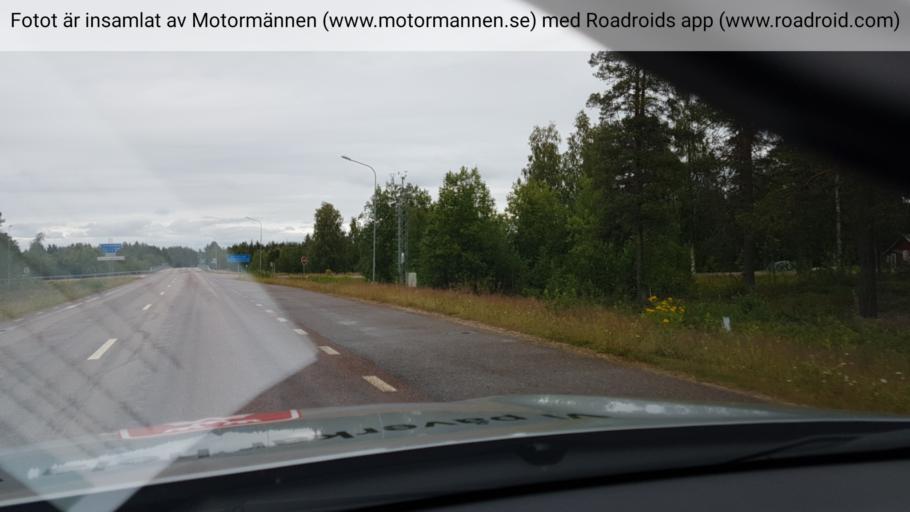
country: SE
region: Norrbotten
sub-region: Pajala Kommun
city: Pajala
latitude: 67.1576
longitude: 22.6313
